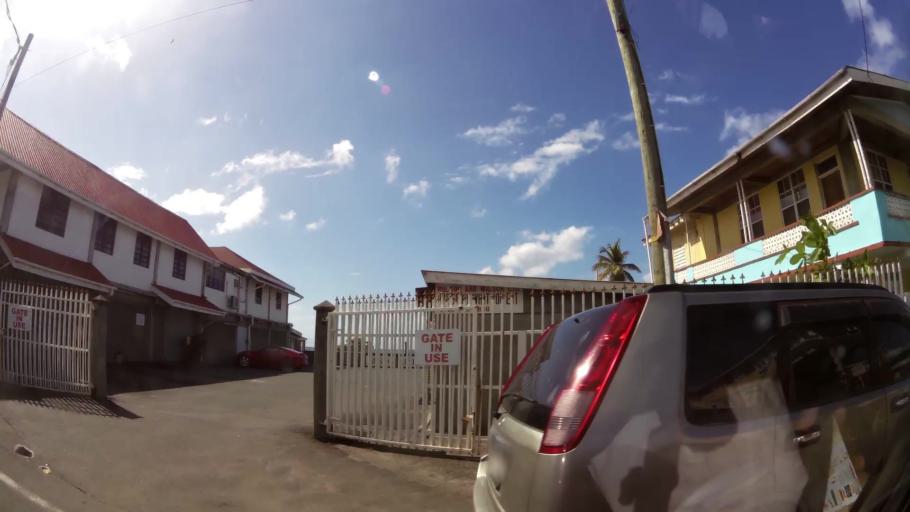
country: DM
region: Saint George
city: Roseau
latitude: 15.3017
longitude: -61.3903
